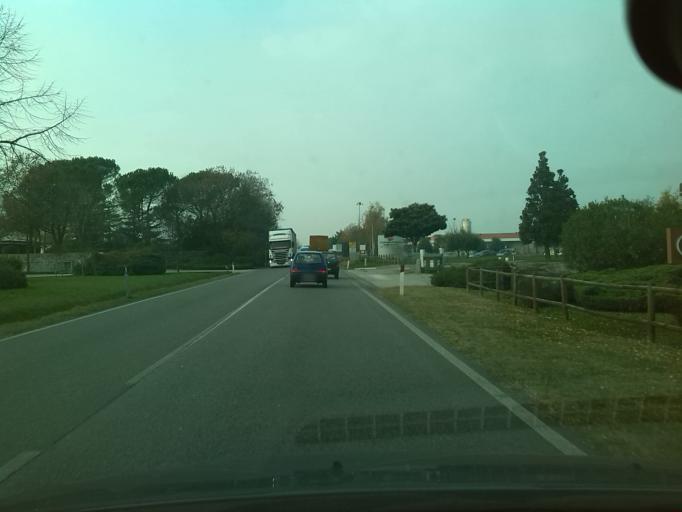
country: IT
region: Friuli Venezia Giulia
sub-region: Provincia di Udine
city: San Giovanni al Natisone
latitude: 45.9668
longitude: 13.4093
